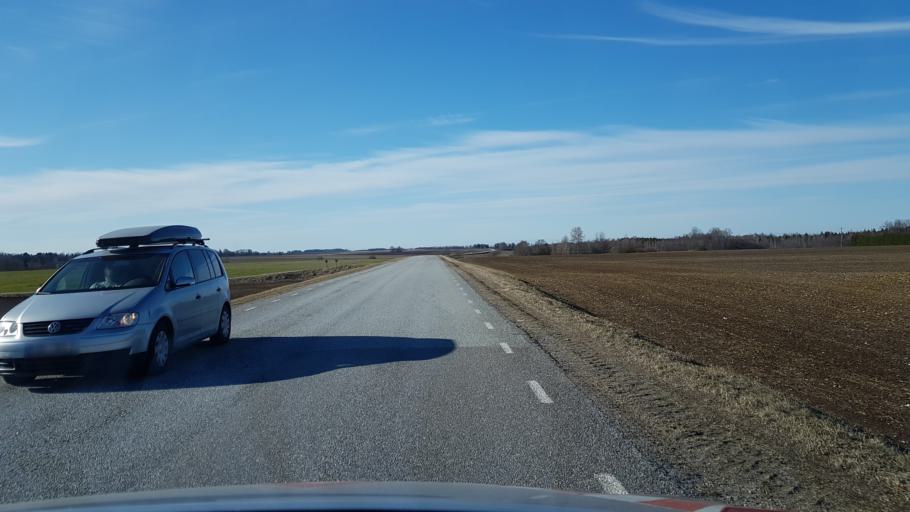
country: EE
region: Laeaene-Virumaa
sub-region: Kadrina vald
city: Kadrina
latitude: 59.3117
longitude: 26.1558
